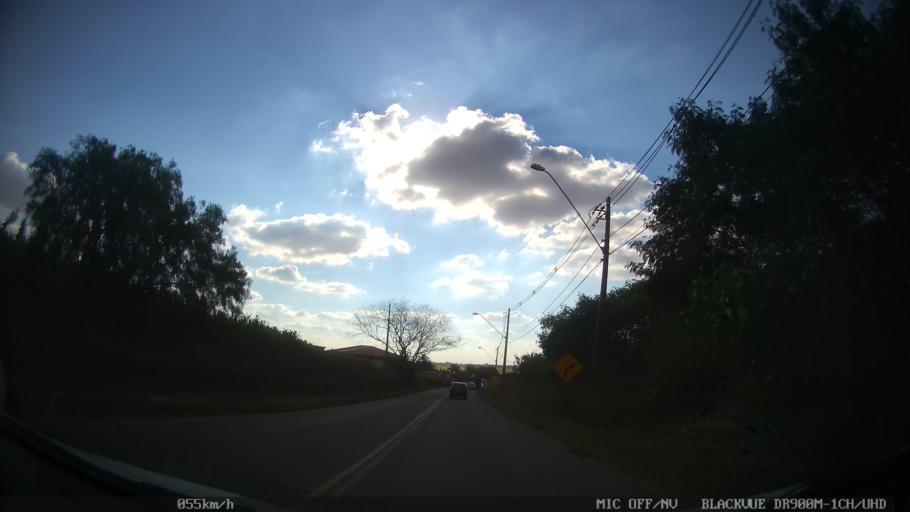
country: BR
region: Sao Paulo
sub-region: Nova Odessa
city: Nova Odessa
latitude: -22.8019
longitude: -47.3351
